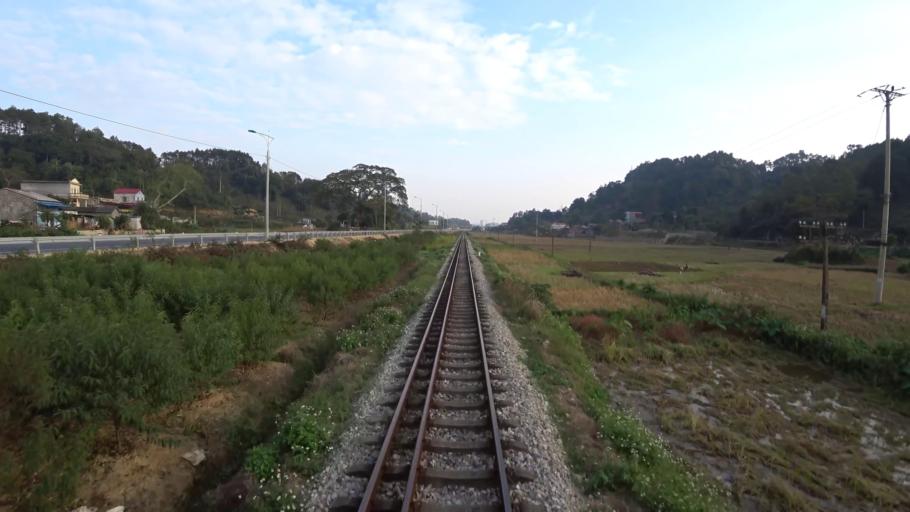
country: VN
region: Lang Son
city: Thi Tran Cao Loc
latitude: 21.9029
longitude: 106.7376
